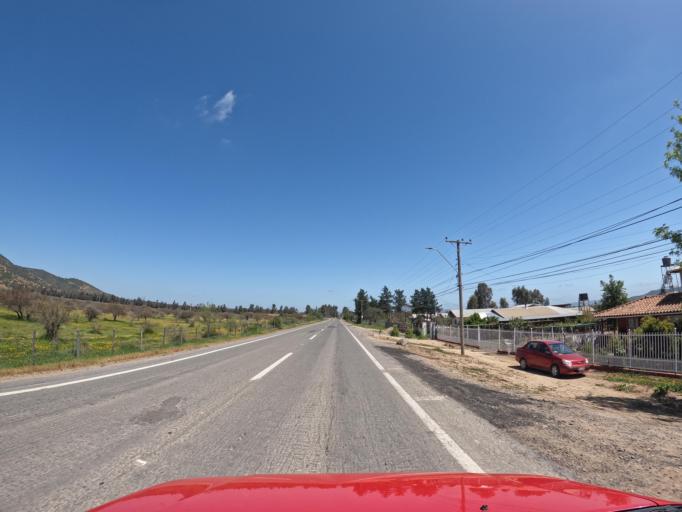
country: CL
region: O'Higgins
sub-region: Provincia de Colchagua
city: Santa Cruz
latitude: -34.7302
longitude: -71.6744
